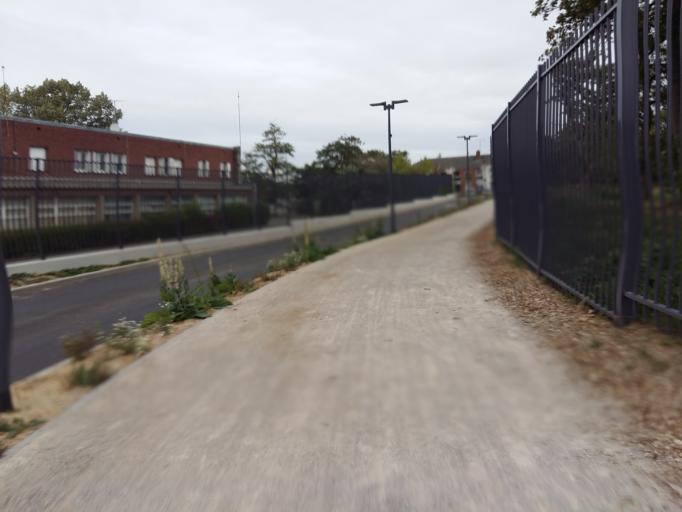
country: FR
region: Picardie
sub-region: Departement de la Somme
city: Amiens
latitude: 49.8767
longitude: 2.2969
